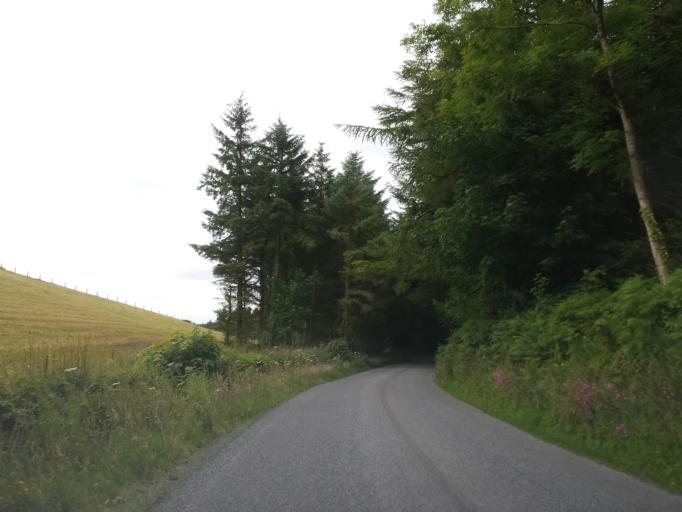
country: GB
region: Scotland
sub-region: Dumfries and Galloway
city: Stranraer
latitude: 54.8541
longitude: -5.1057
